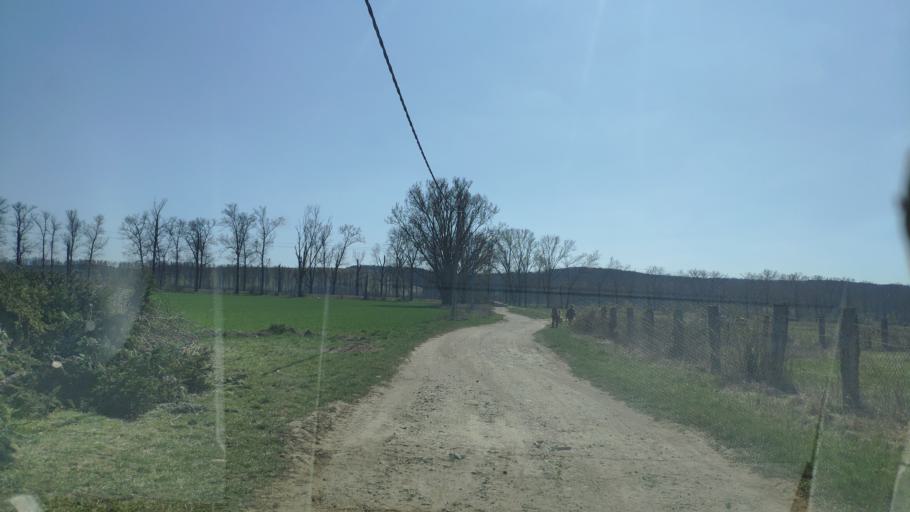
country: SK
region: Kosicky
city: Moldava nad Bodvou
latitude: 48.5752
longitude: 20.9477
